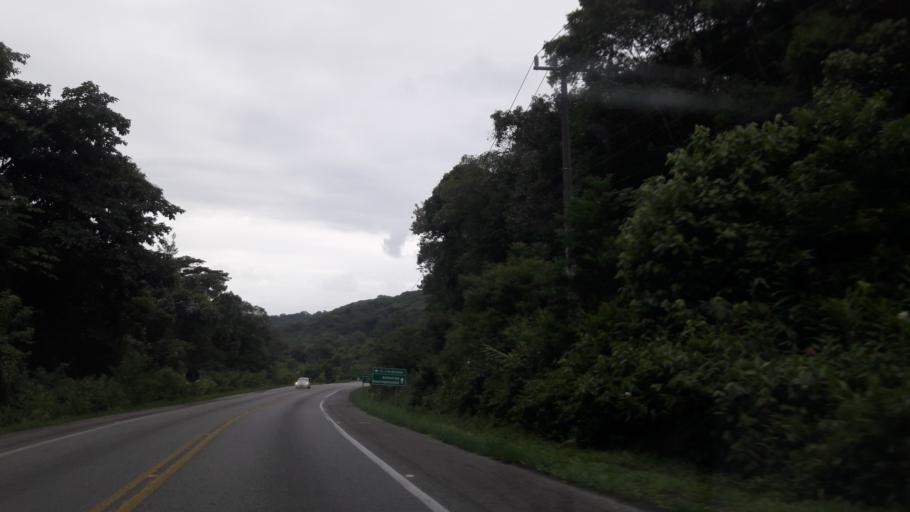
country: BR
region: Parana
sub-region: Antonina
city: Antonina
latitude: -25.4430
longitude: -48.7876
